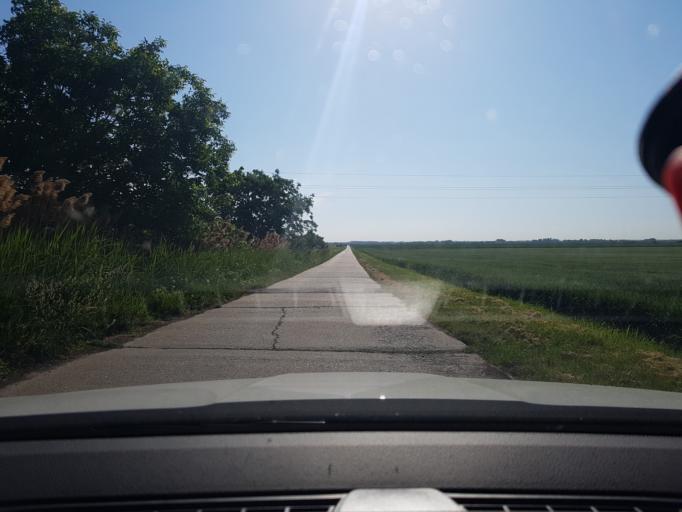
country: HU
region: Tolna
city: Szekszard
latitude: 46.2840
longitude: 18.6857
